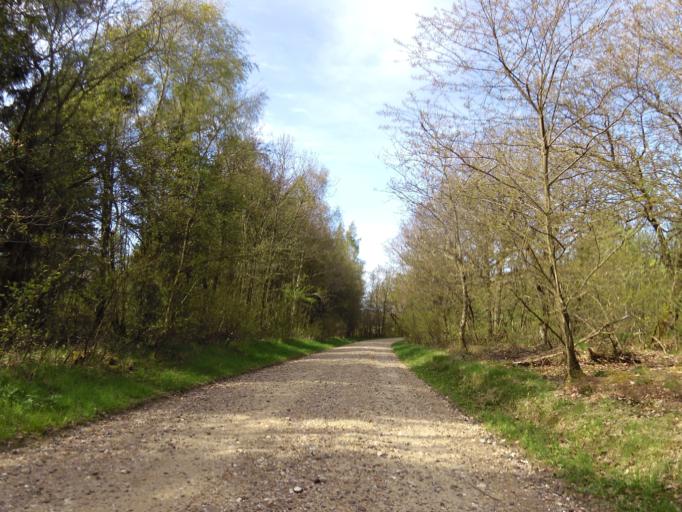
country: DK
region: Central Jutland
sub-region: Holstebro Kommune
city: Vinderup
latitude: 56.4787
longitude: 8.8721
